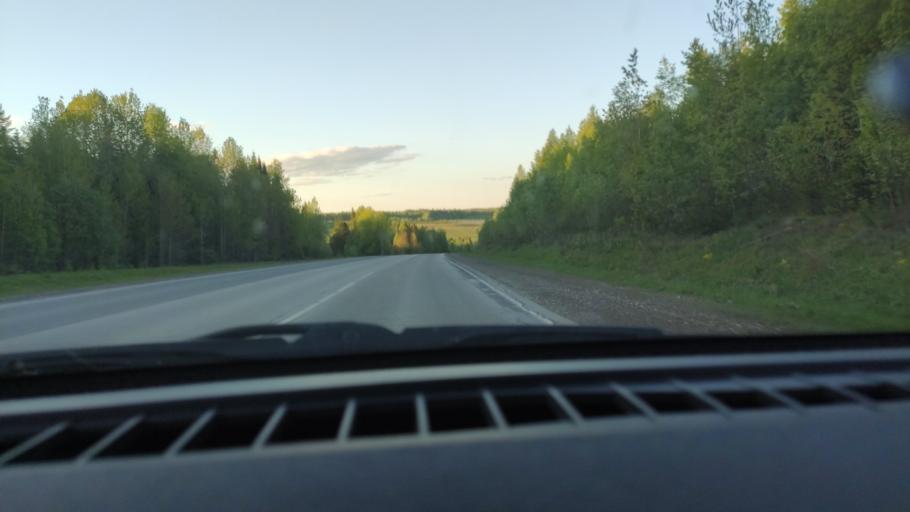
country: RU
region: Perm
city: Dobryanka
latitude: 58.4288
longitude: 56.5340
